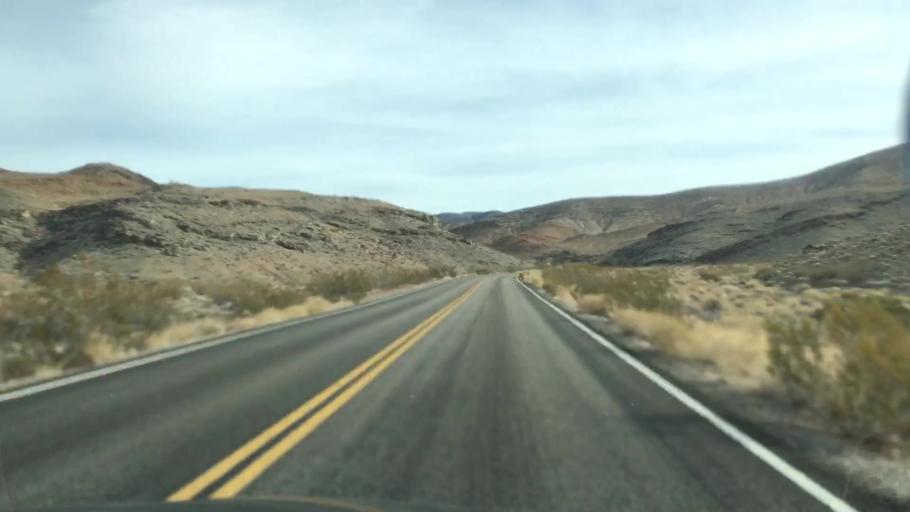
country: US
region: Nevada
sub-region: Nye County
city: Beatty
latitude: 36.7426
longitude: -116.9627
